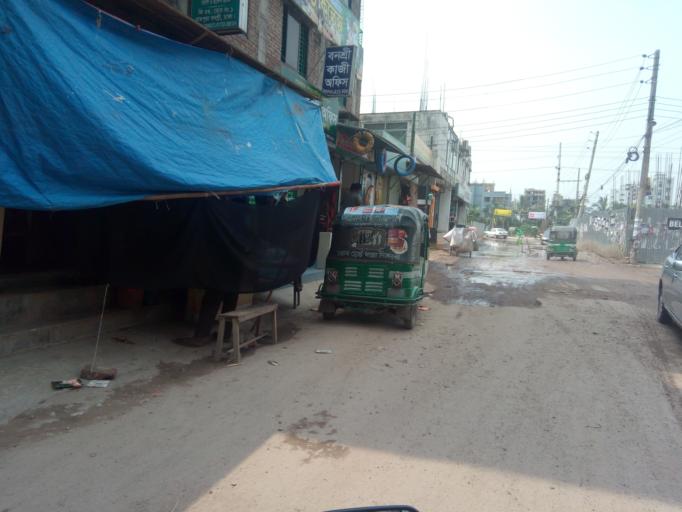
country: BD
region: Dhaka
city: Paltan
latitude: 23.7615
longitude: 90.4427
